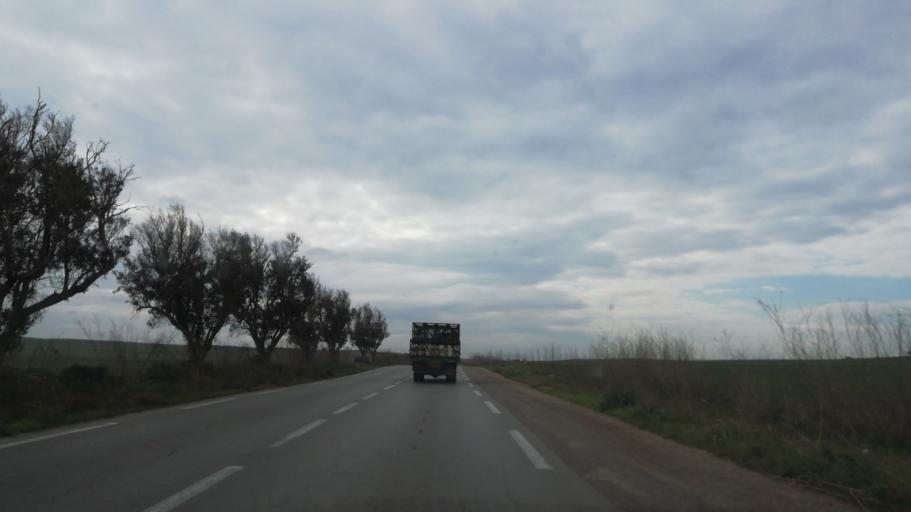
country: DZ
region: Oran
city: Ain el Bya
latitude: 35.7604
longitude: -0.3500
